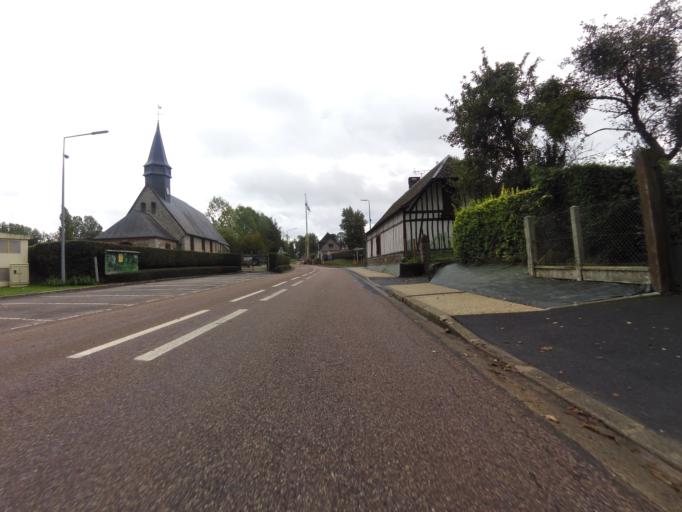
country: FR
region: Haute-Normandie
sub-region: Departement de la Seine-Maritime
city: Totes
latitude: 49.7056
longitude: 1.0263
